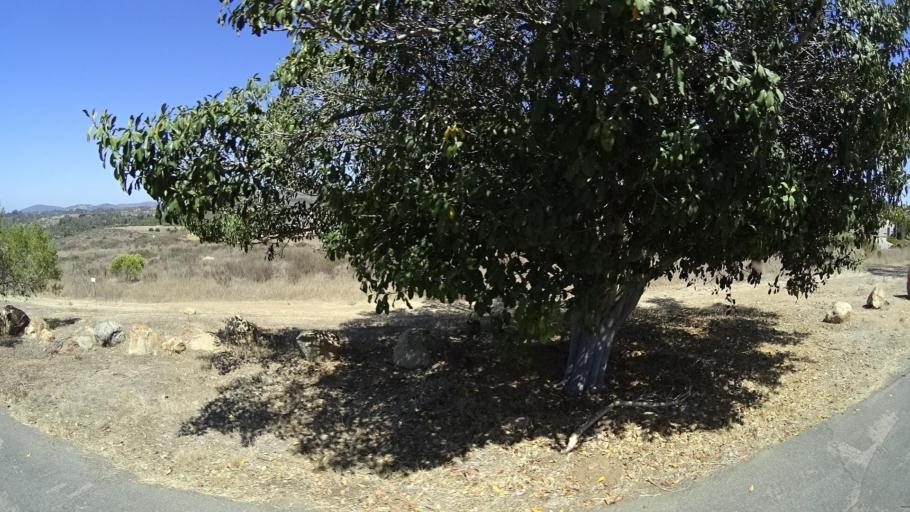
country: US
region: California
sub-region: San Diego County
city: Fairbanks Ranch
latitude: 33.0201
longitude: -117.1722
